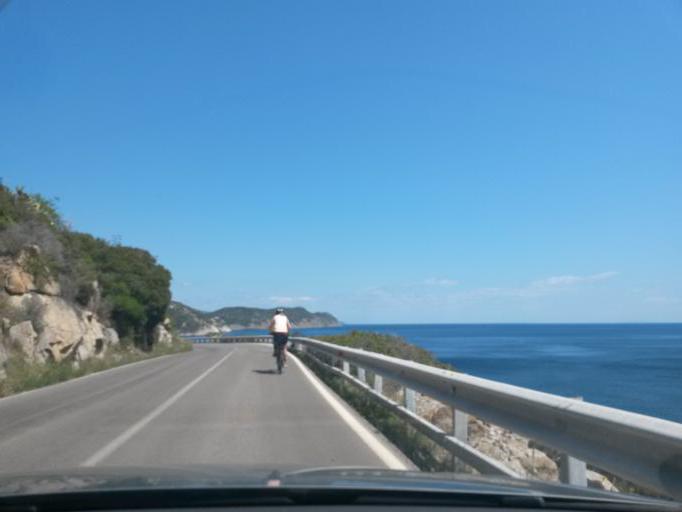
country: IT
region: Tuscany
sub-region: Provincia di Livorno
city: Marciana
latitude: 42.7326
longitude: 10.1640
